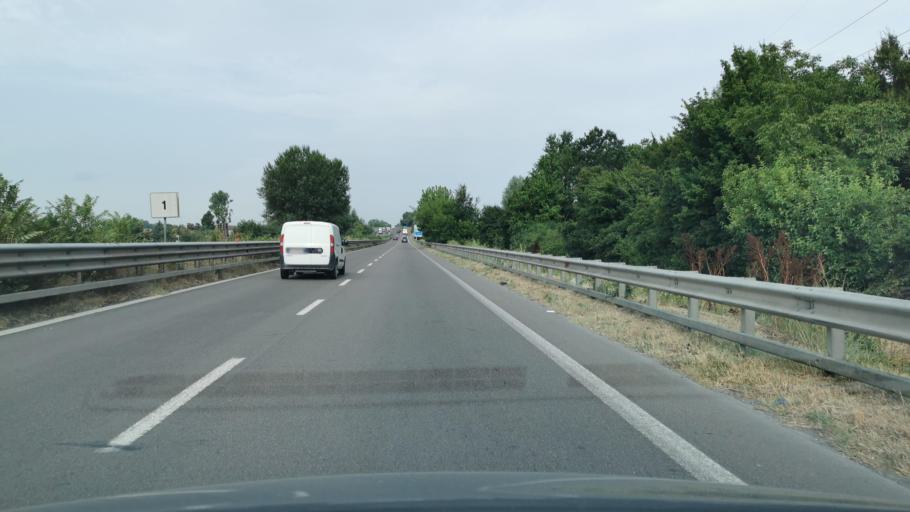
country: IT
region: Emilia-Romagna
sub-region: Provincia di Modena
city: Villanova
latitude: 44.6724
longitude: 10.9195
